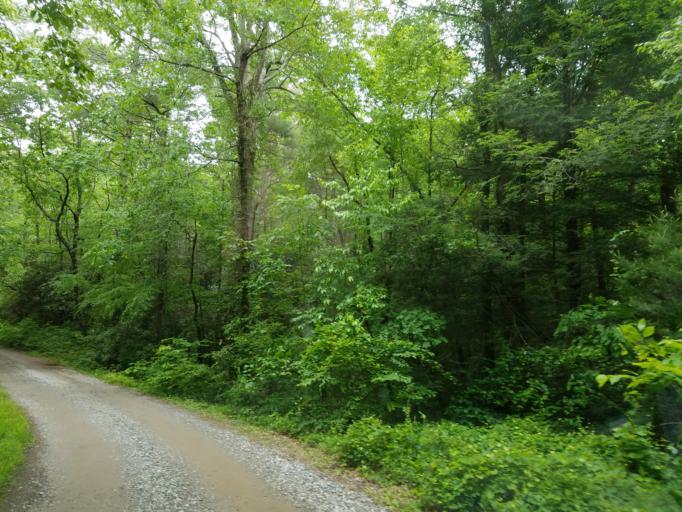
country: US
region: Georgia
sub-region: Lumpkin County
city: Dahlonega
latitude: 34.6724
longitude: -83.9766
